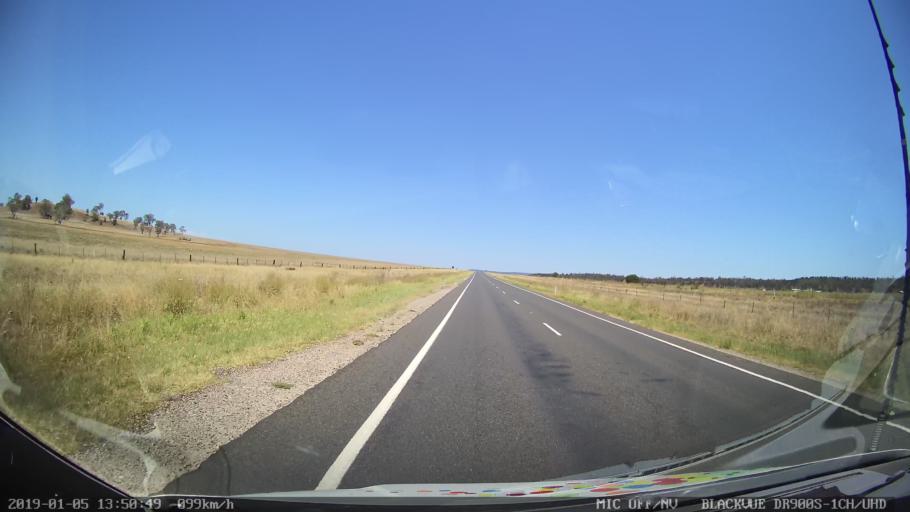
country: AU
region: New South Wales
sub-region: Gunnedah
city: Gunnedah
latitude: -31.0355
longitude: 150.2755
